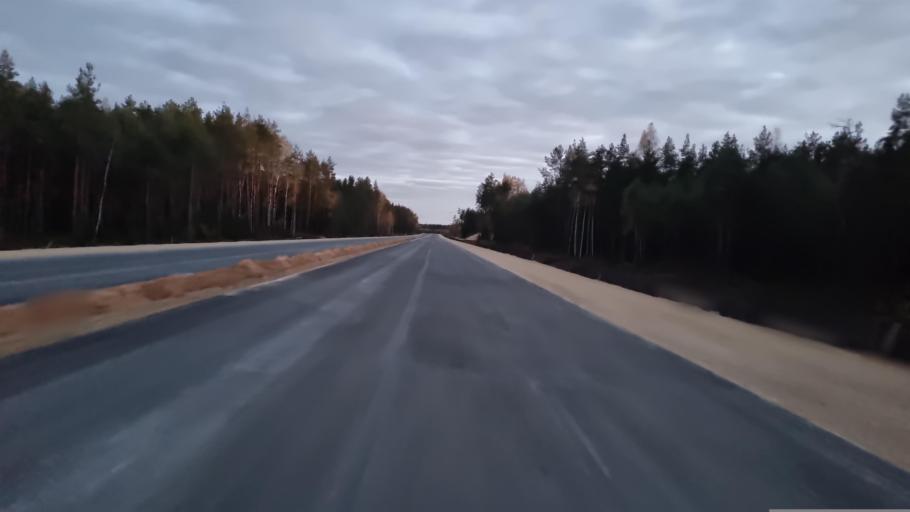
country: LV
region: Kekava
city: Balozi
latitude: 56.8493
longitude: 24.1569
